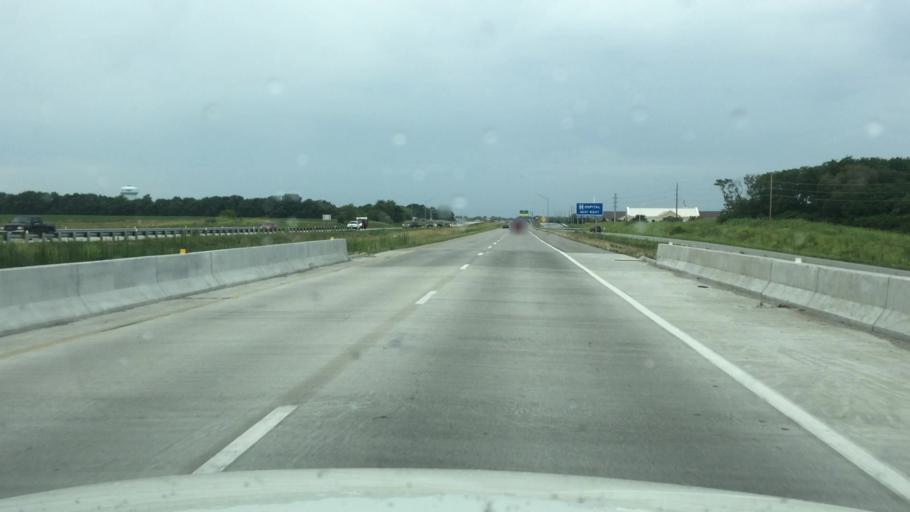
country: US
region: Missouri
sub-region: Jackson County
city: Greenwood
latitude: 38.9018
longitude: -94.3187
